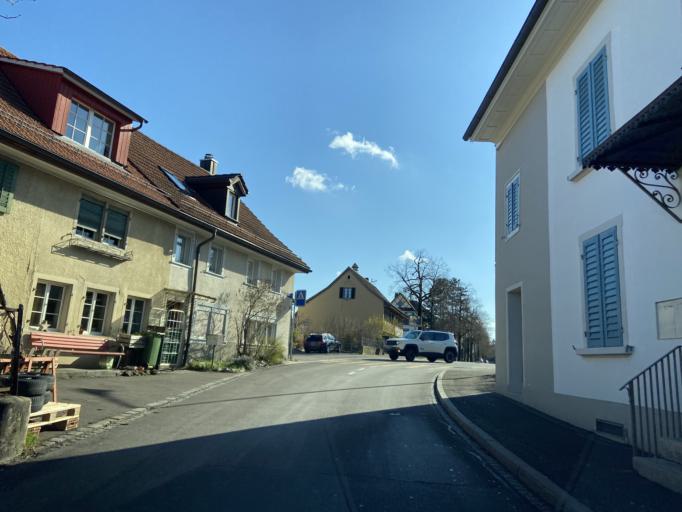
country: CH
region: Zurich
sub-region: Bezirk Winterthur
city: Wuelflingen (Kreis 6) / Lindenplatz
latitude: 47.5093
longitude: 8.6955
